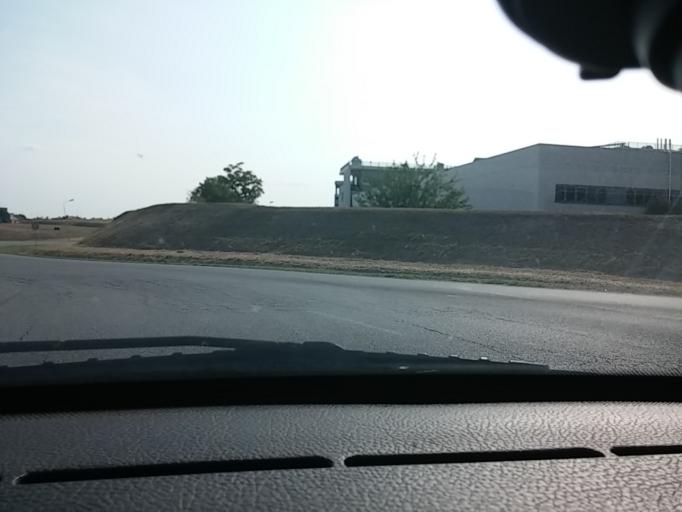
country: IT
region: Emilia-Romagna
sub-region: Provincia di Ferrara
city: Ferrara
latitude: 44.8350
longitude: 11.6011
